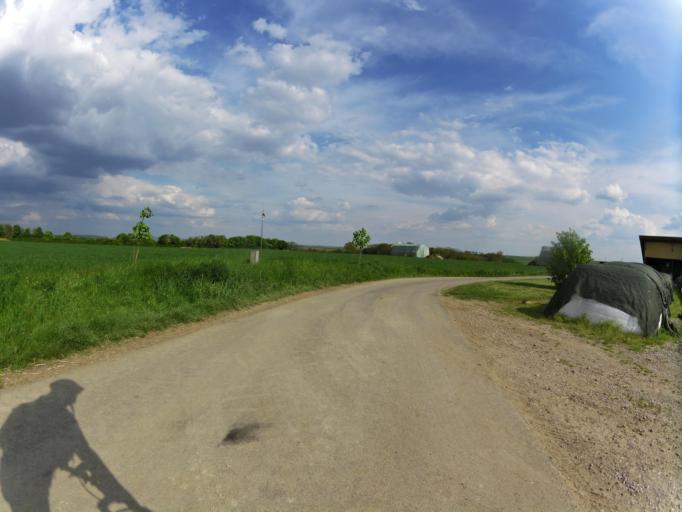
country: DE
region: Bavaria
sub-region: Regierungsbezirk Unterfranken
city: Giebelstadt
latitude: 49.6307
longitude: 9.9487
